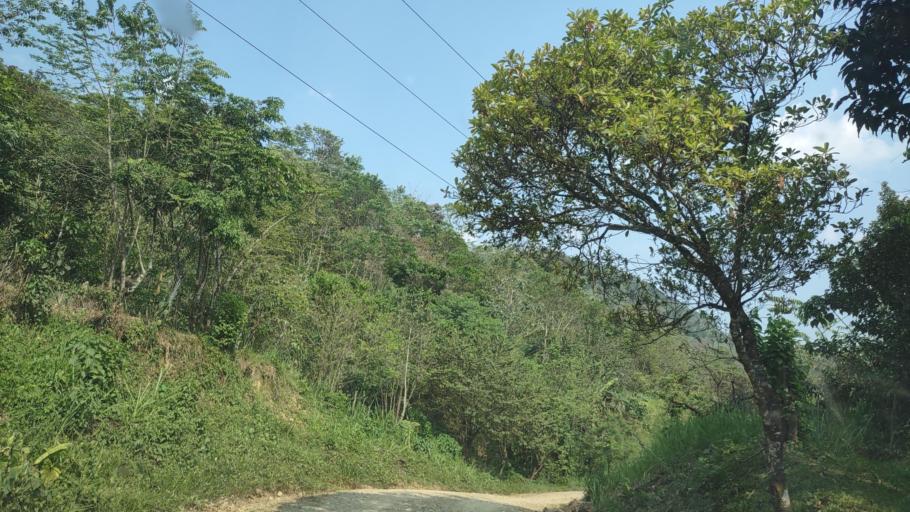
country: MX
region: Chiapas
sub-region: Tecpatan
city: Raudales Malpaso
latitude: 17.3225
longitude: -93.7437
